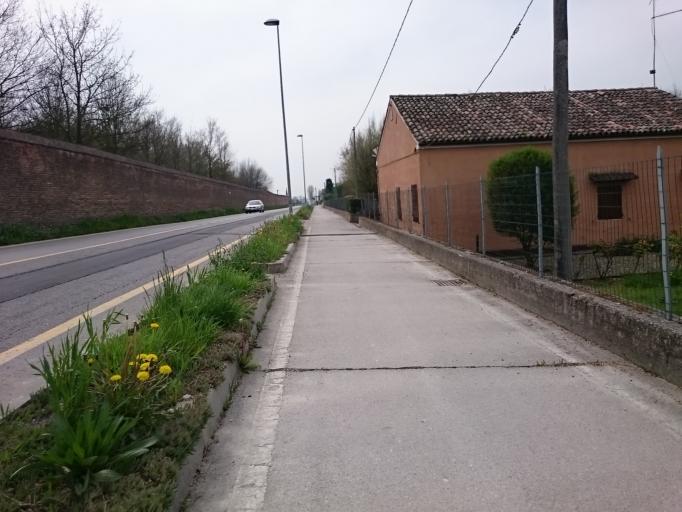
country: IT
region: Veneto
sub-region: Provincia di Padova
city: Bagnoli di Sopra
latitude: 45.1812
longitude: 11.8811
